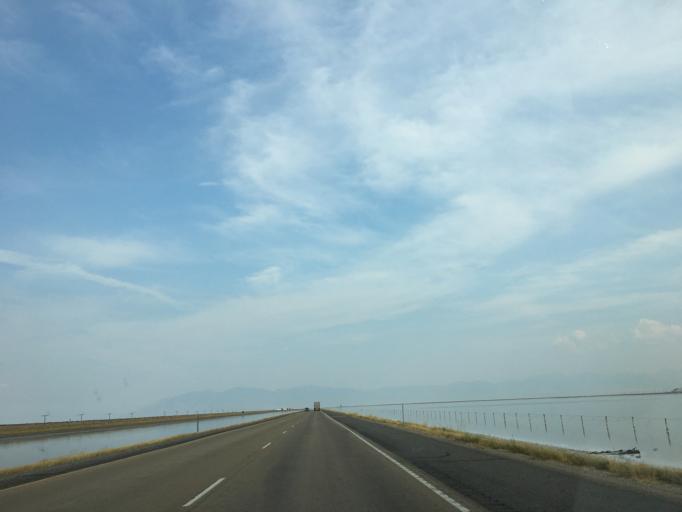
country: US
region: Utah
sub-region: Tooele County
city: Grantsville
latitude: 40.7357
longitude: -112.6089
